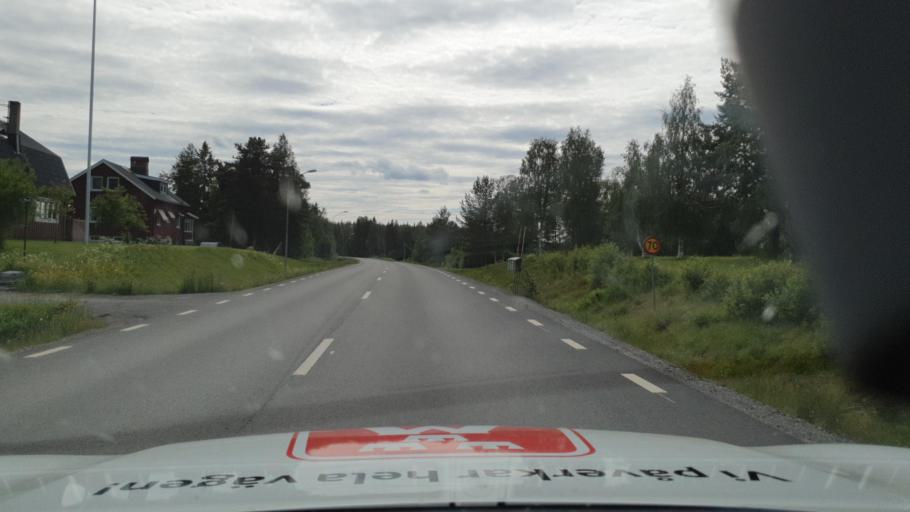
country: SE
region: Vaesterbotten
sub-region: Norsjo Kommun
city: Norsjoe
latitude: 64.9036
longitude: 19.4759
